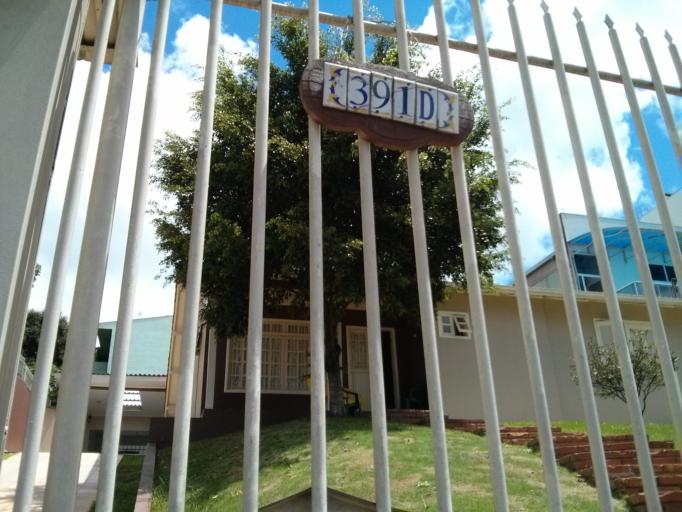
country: BR
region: Santa Catarina
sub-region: Chapeco
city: Chapeco
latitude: -27.1025
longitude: -52.6202
